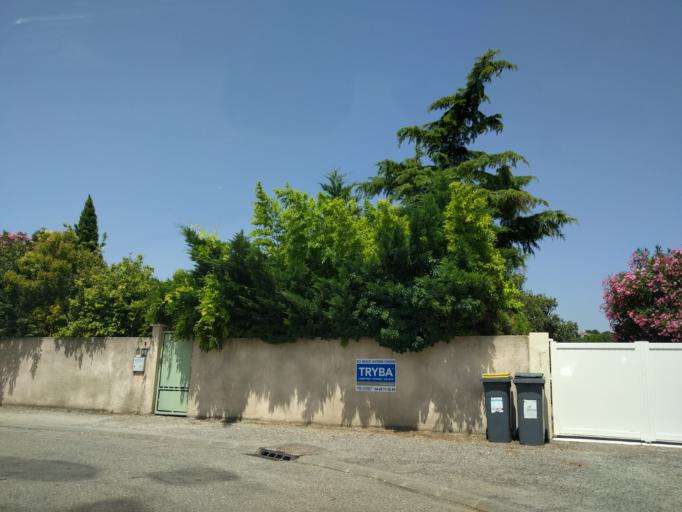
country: FR
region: Languedoc-Roussillon
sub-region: Departement de l'Aude
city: Carcassonne
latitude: 43.2192
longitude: 2.3598
